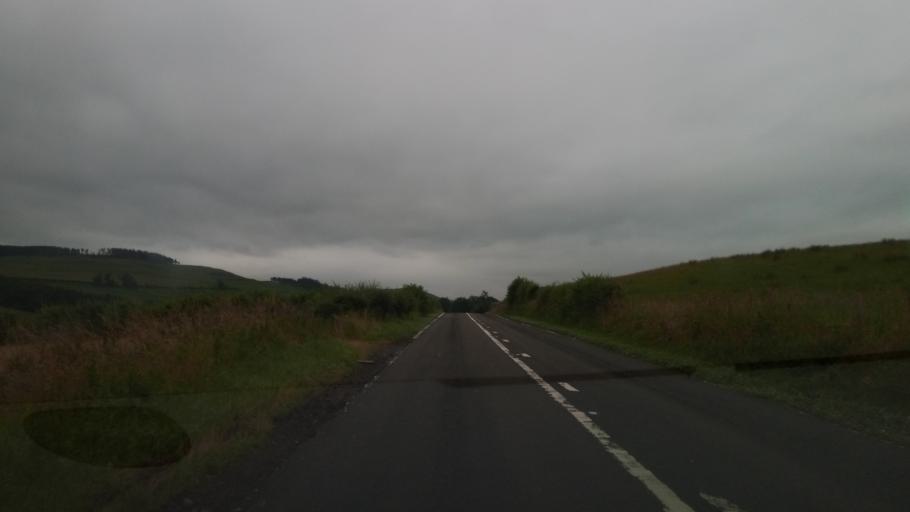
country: GB
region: Scotland
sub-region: The Scottish Borders
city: Hawick
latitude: 55.3730
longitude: -2.8772
